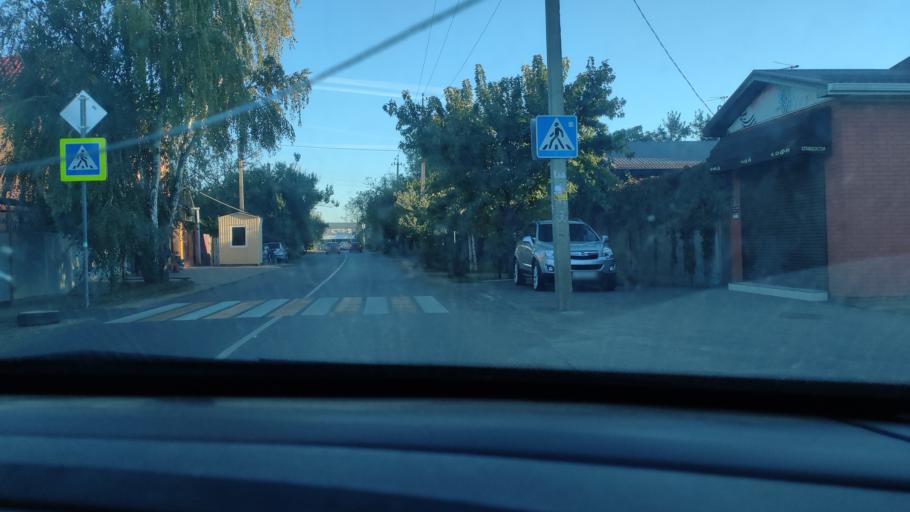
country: RU
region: Adygeya
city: Yablonovskiy
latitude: 45.0376
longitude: 38.9244
